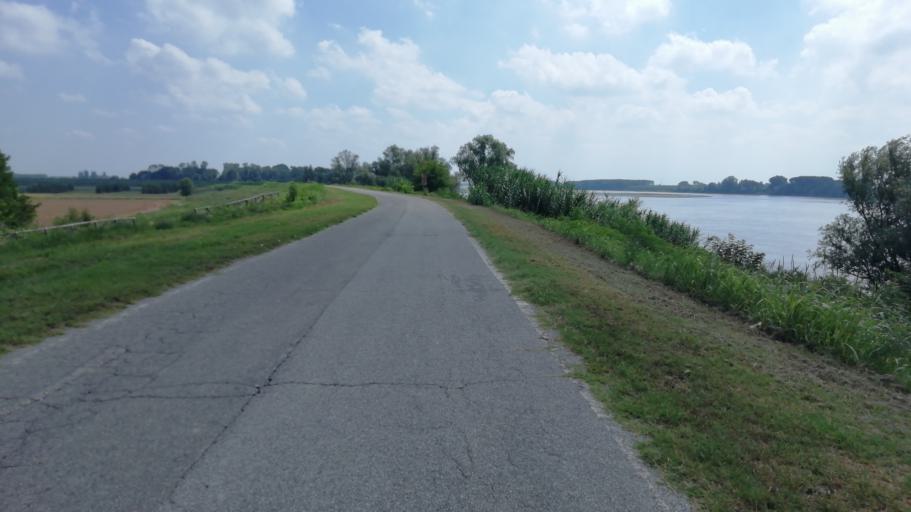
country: IT
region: Veneto
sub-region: Provincia di Rovigo
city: Gaiba
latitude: 44.9397
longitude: 11.4846
